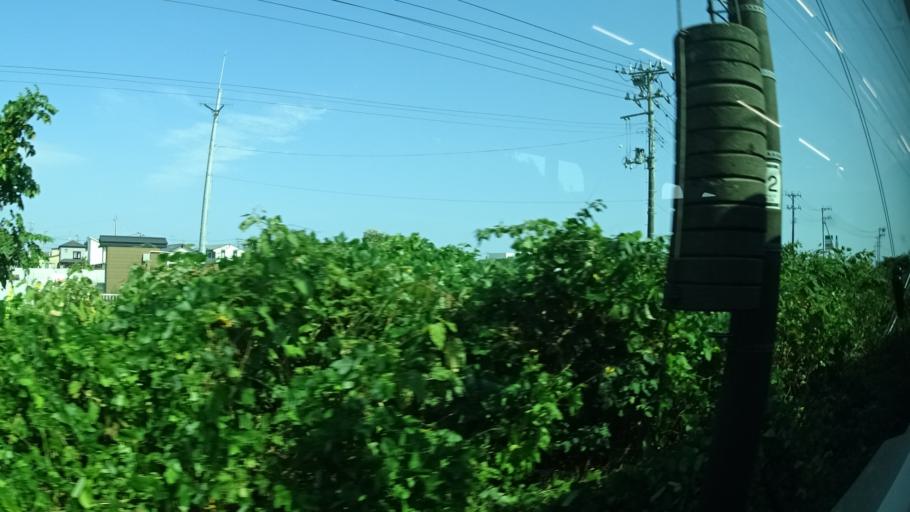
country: JP
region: Miyagi
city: Matsushima
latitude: 38.3840
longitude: 141.0674
